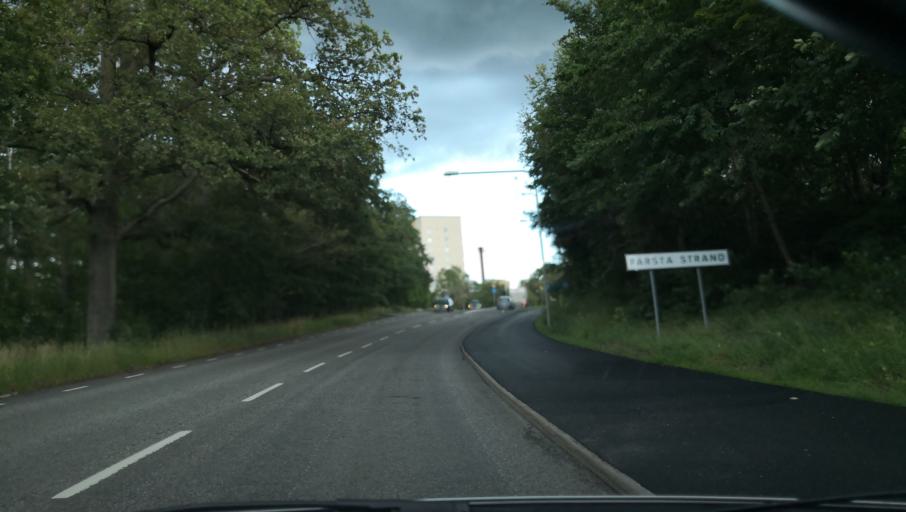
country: SE
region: Stockholm
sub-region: Stockholms Kommun
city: Arsta
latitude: 59.2389
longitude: 18.0906
